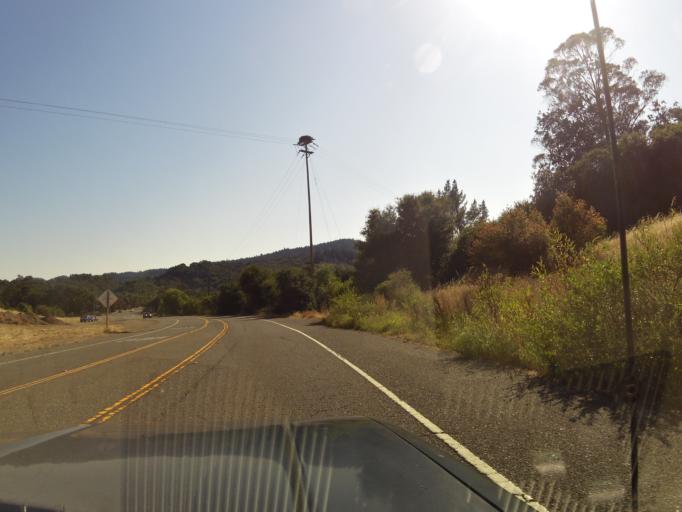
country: US
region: California
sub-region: Sonoma County
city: Cloverdale
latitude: 38.8280
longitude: -123.0148
